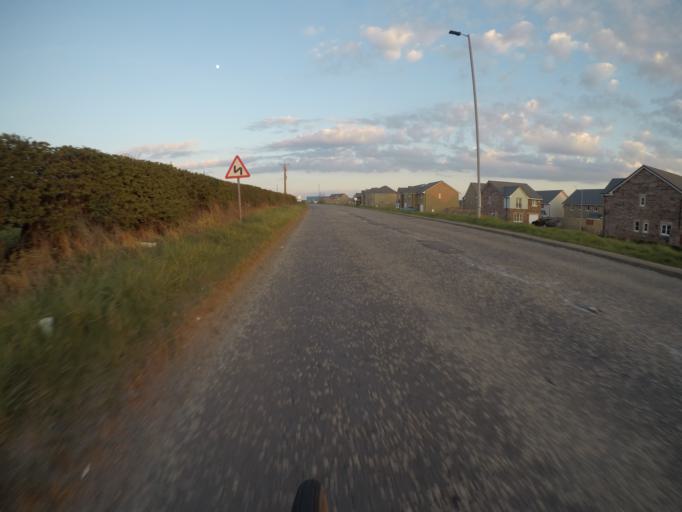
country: GB
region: Scotland
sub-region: South Ayrshire
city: Troon
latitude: 55.5639
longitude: -4.6364
